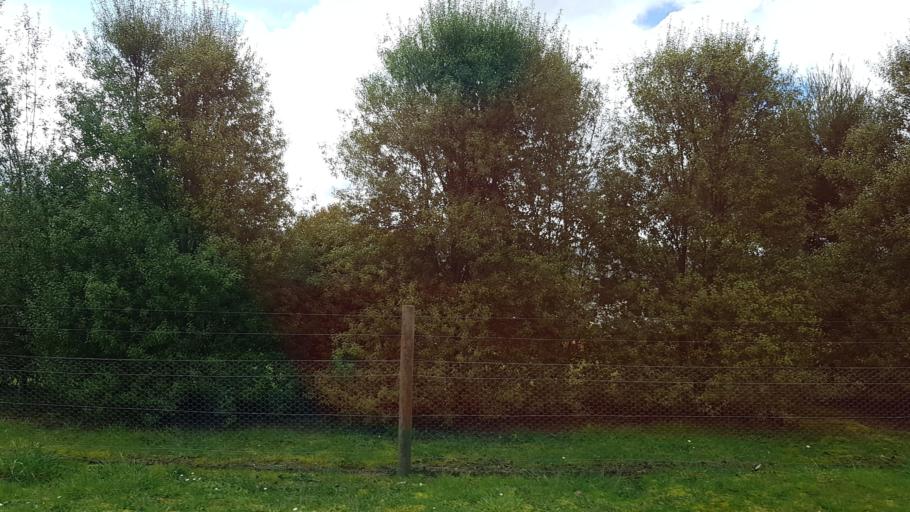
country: AU
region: Tasmania
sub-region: Huon Valley
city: Huonville
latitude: -43.0005
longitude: 147.0662
